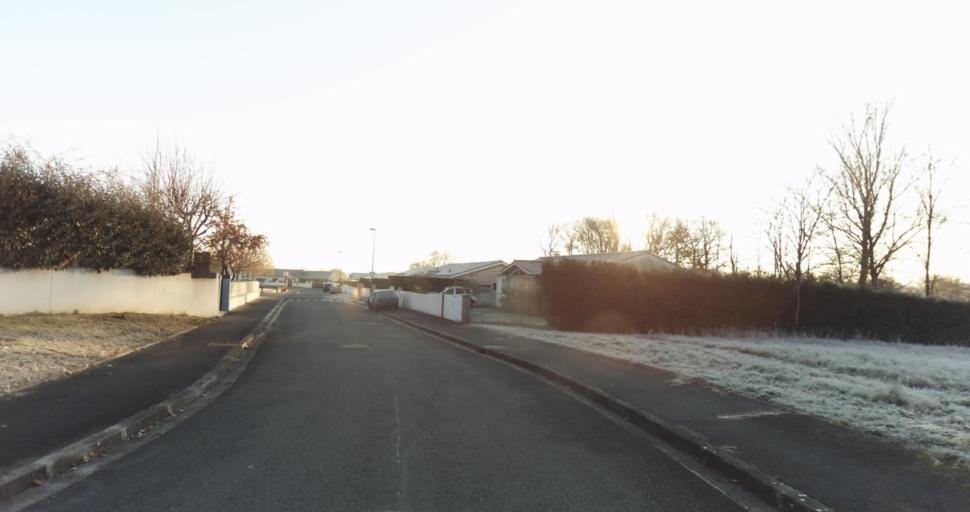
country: FR
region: Aquitaine
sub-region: Departement de la Gironde
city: Ambares-et-Lagrave
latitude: 44.9139
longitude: -0.4968
